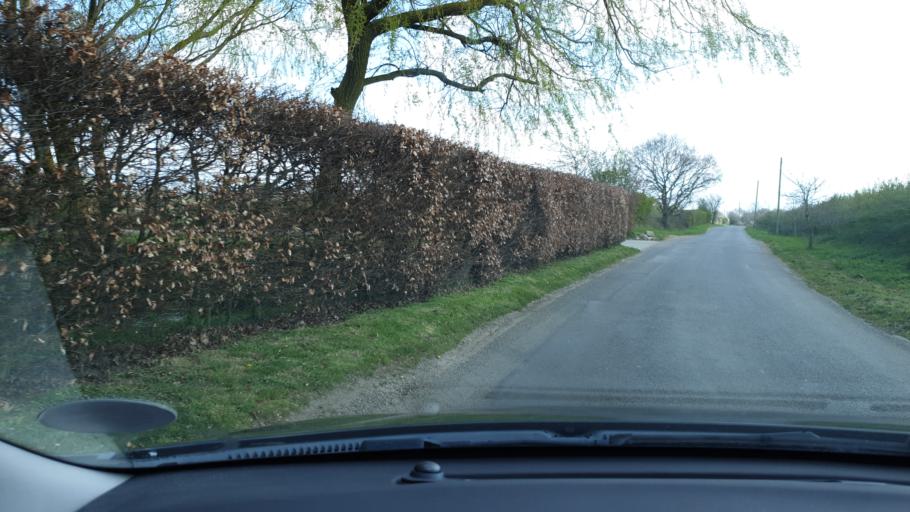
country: GB
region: England
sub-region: Essex
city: Great Bentley
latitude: 51.8409
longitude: 1.0873
